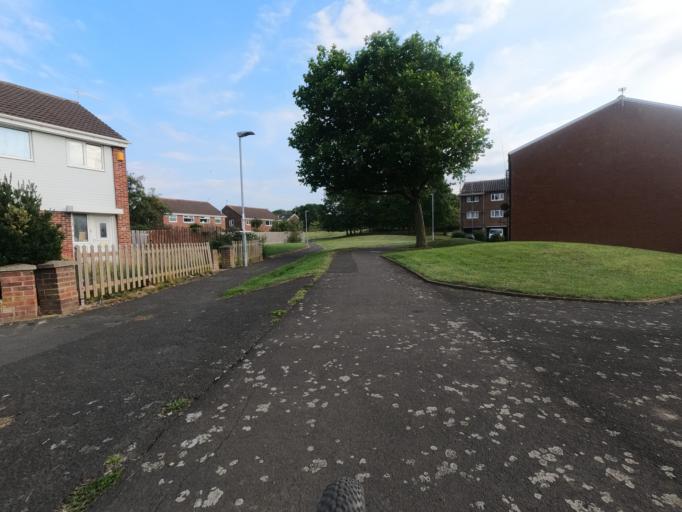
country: GB
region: England
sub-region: Northumberland
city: Cramlington
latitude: 55.0870
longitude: -1.6094
